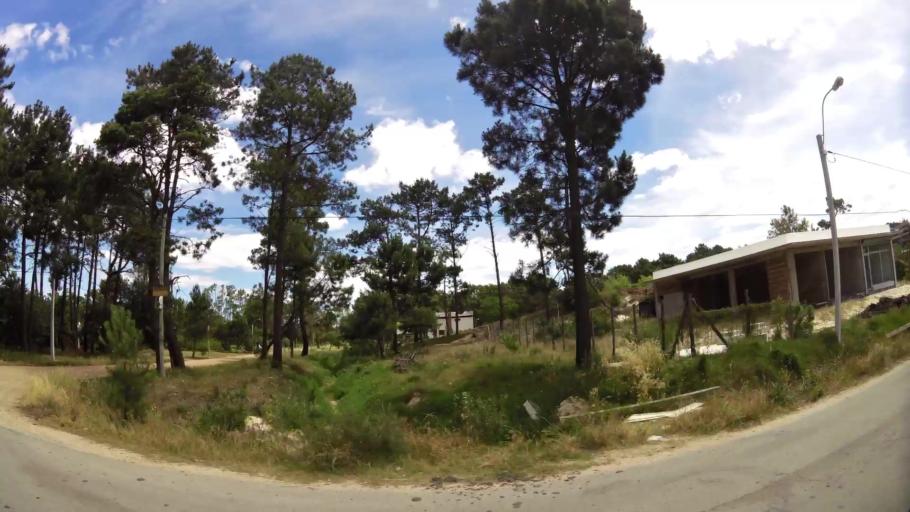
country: UY
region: Canelones
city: Empalme Olmos
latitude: -34.7898
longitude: -55.8893
